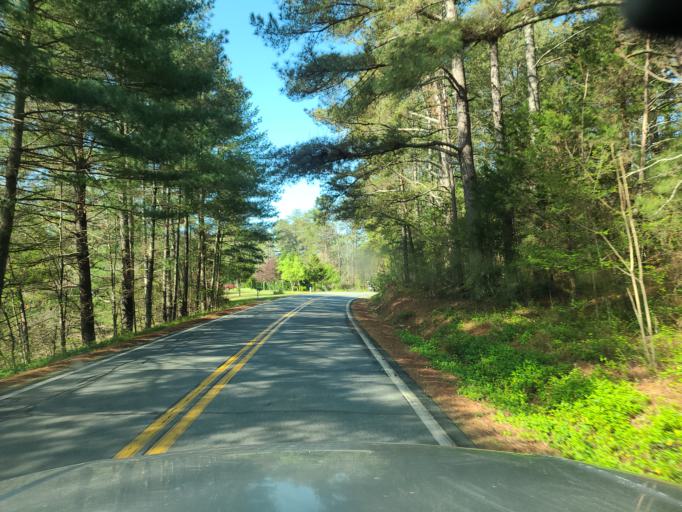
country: US
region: North Carolina
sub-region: Rutherford County
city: Forest City
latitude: 35.4093
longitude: -81.8613
